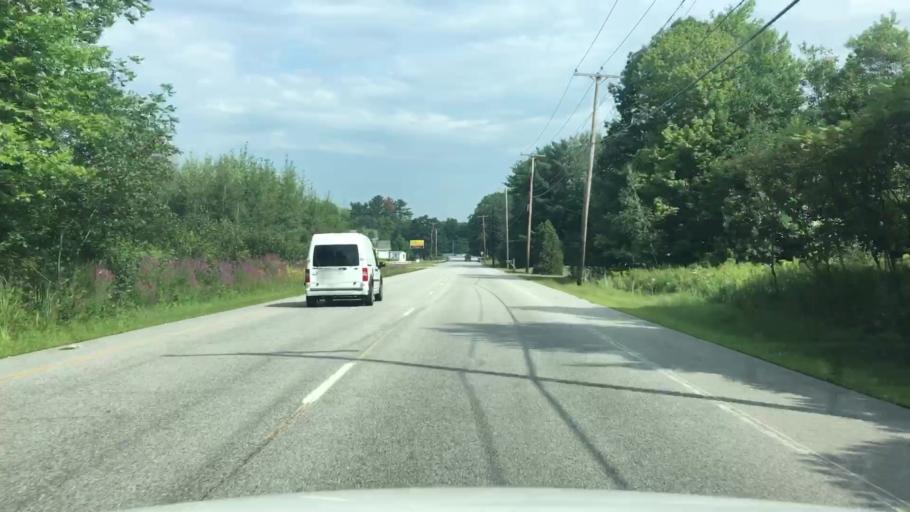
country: US
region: Maine
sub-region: Androscoggin County
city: Auburn
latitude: 44.0564
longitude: -70.2532
